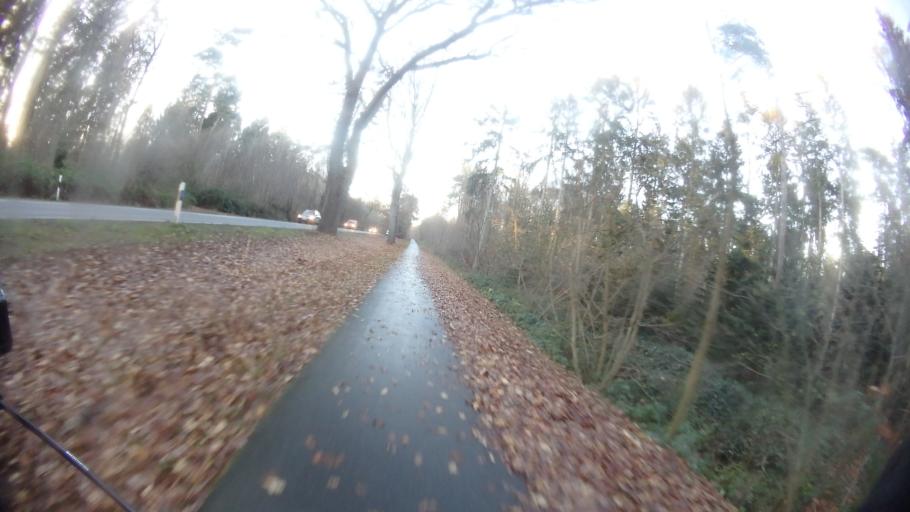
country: DE
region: Schleswig-Holstein
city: Ratekau
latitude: 53.9947
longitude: 10.7075
